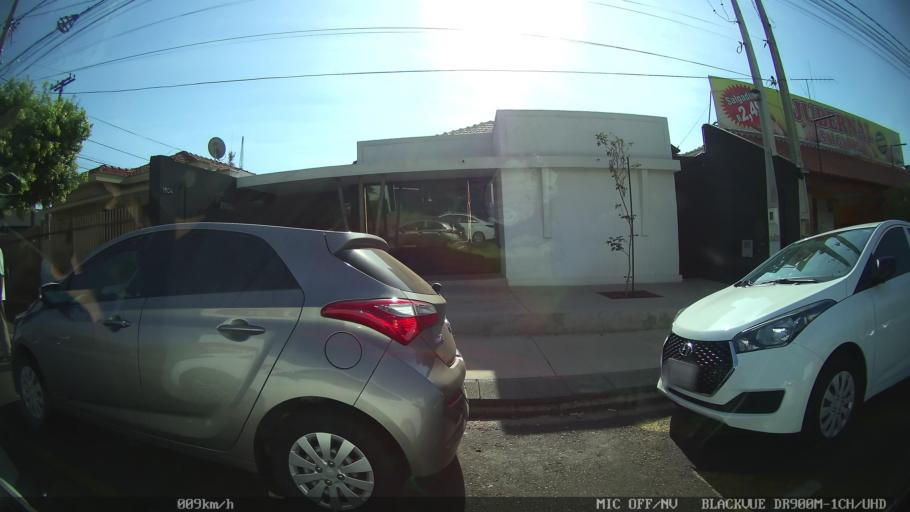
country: BR
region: Sao Paulo
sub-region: Sao Jose Do Rio Preto
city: Sao Jose do Rio Preto
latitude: -20.8021
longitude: -49.3887
